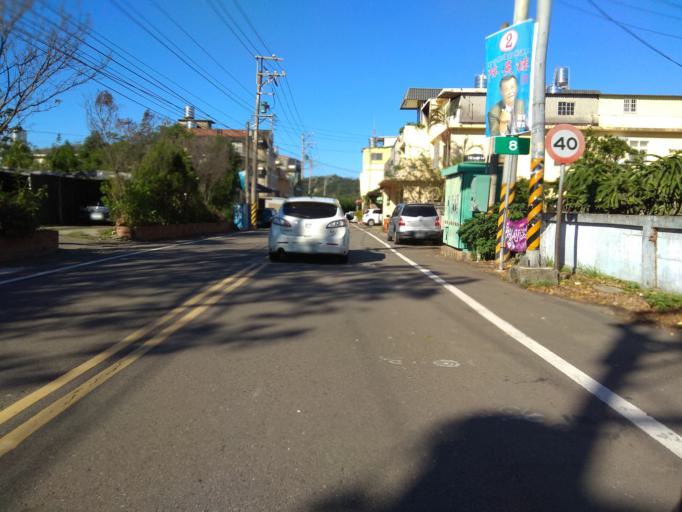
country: TW
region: Taiwan
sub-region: Hsinchu
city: Zhubei
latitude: 24.8469
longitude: 121.1155
